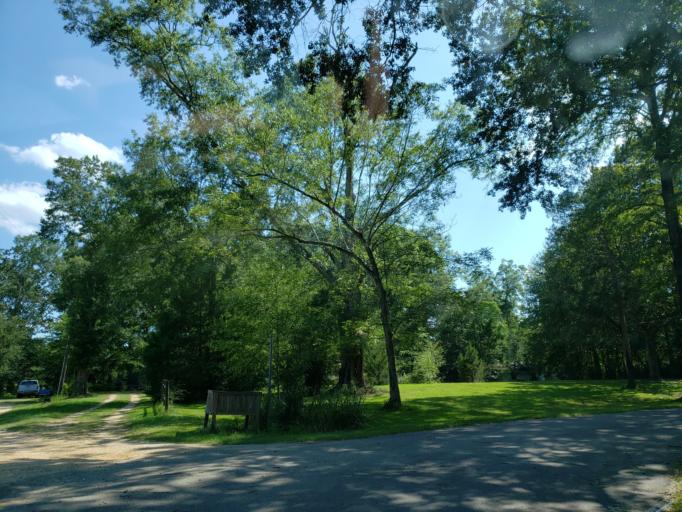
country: US
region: Mississippi
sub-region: Lamar County
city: Sumrall
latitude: 31.4166
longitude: -89.5401
